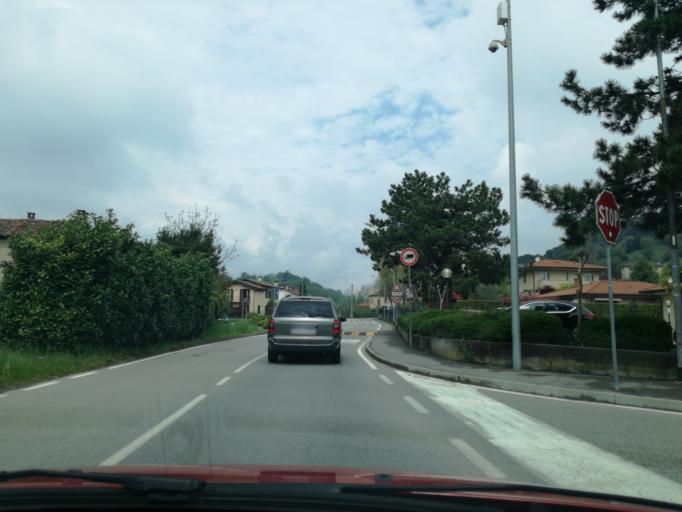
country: IT
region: Lombardy
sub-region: Provincia di Lecco
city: Canova-San Zeno
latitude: 45.7203
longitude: 9.3964
